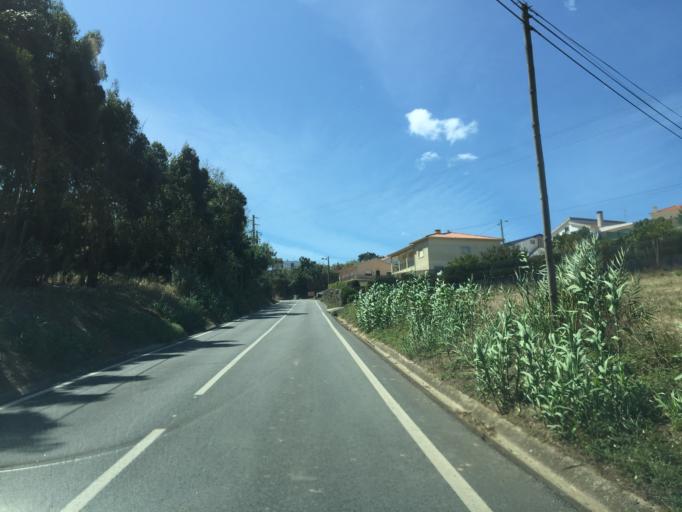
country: PT
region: Lisbon
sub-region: Lourinha
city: Lourinha
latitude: 39.2591
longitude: -9.3141
